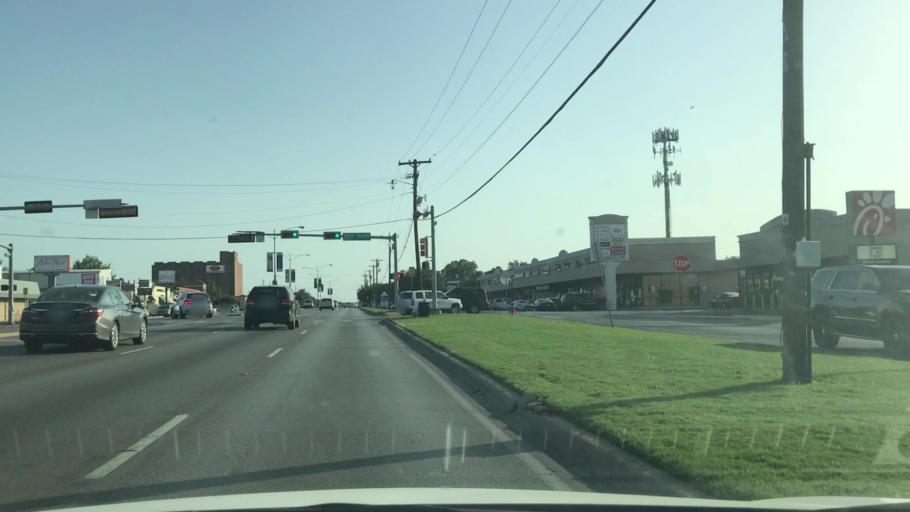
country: US
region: Texas
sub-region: Dallas County
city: Highland Park
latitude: 32.8289
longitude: -96.7082
